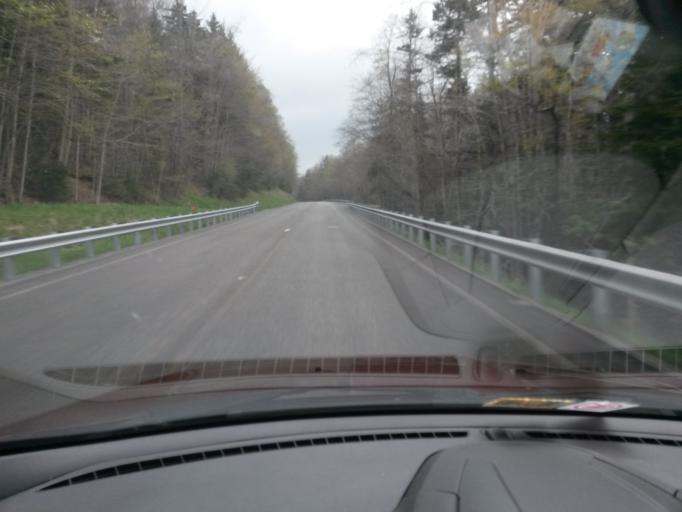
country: US
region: West Virginia
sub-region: Randolph County
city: Elkins
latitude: 38.6263
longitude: -79.9000
